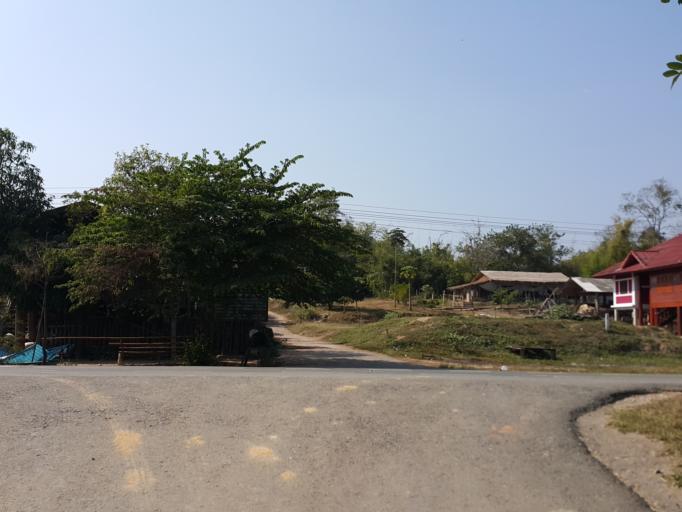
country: TH
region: Lampang
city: Wang Nuea
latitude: 19.0047
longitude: 99.6122
